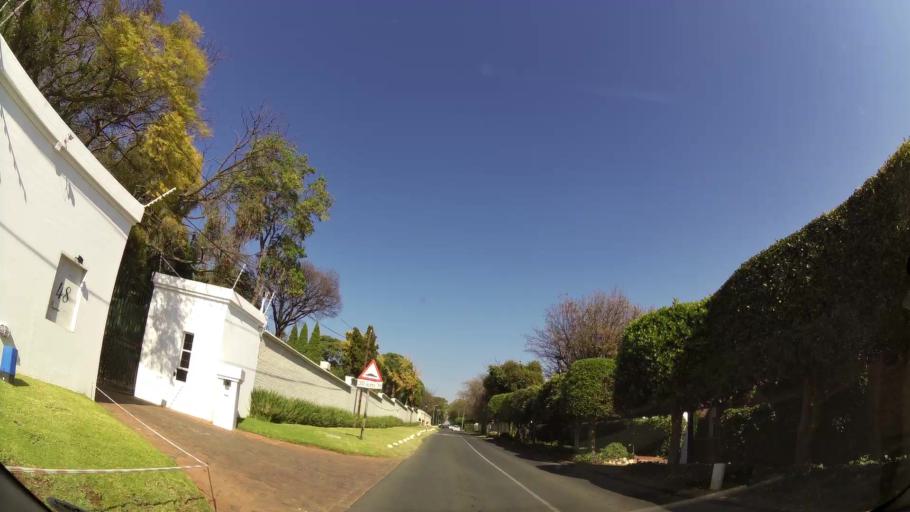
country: ZA
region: Gauteng
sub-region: City of Johannesburg Metropolitan Municipality
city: Johannesburg
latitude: -26.1095
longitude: 28.0364
